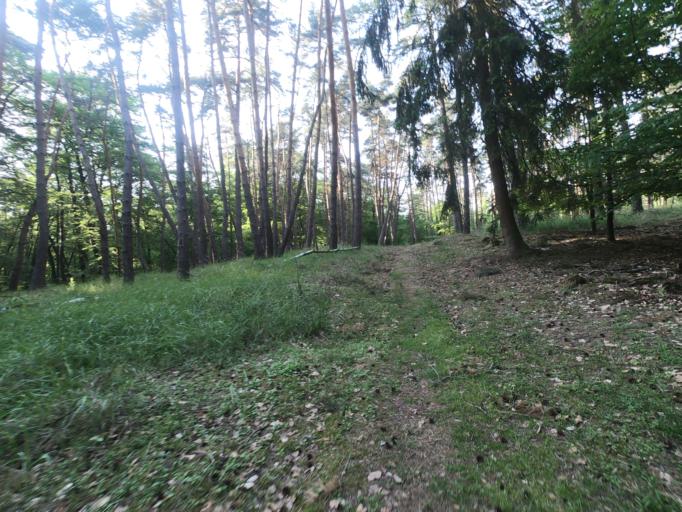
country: DE
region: Hesse
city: Kelsterbach
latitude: 50.0178
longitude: 8.5425
